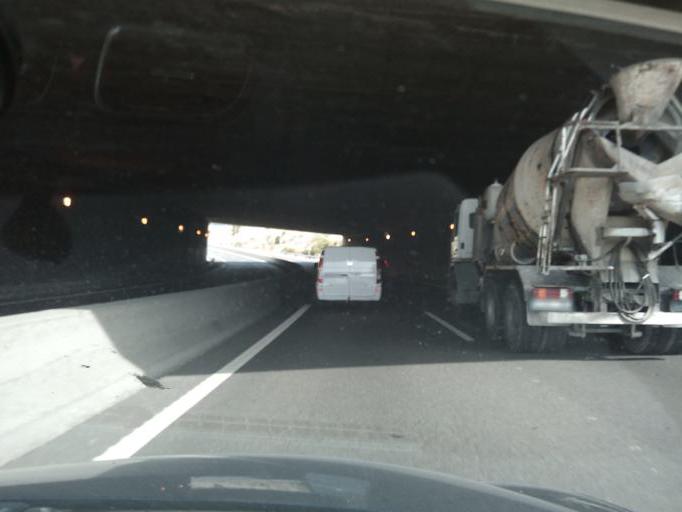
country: ES
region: Madrid
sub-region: Provincia de Madrid
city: Barajas de Madrid
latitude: 40.4673
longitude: -3.5817
